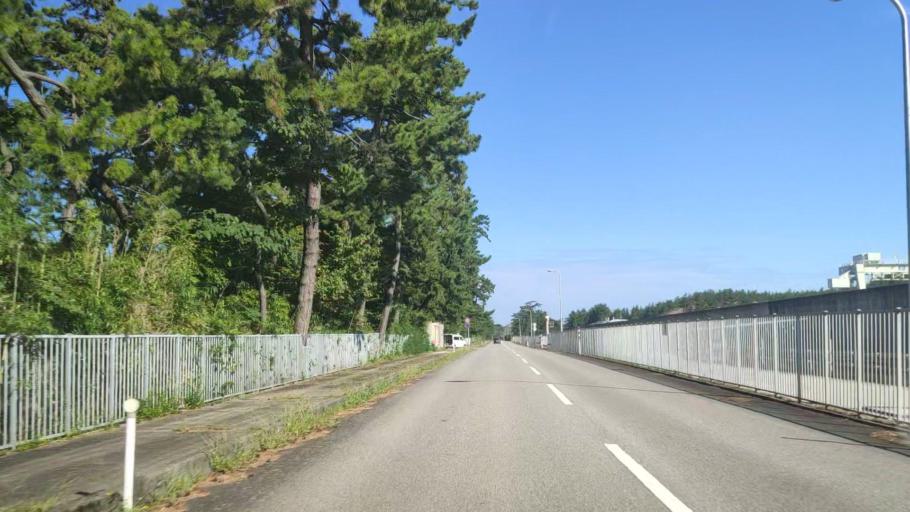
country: JP
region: Ishikawa
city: Hakui
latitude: 37.0600
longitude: 136.7236
